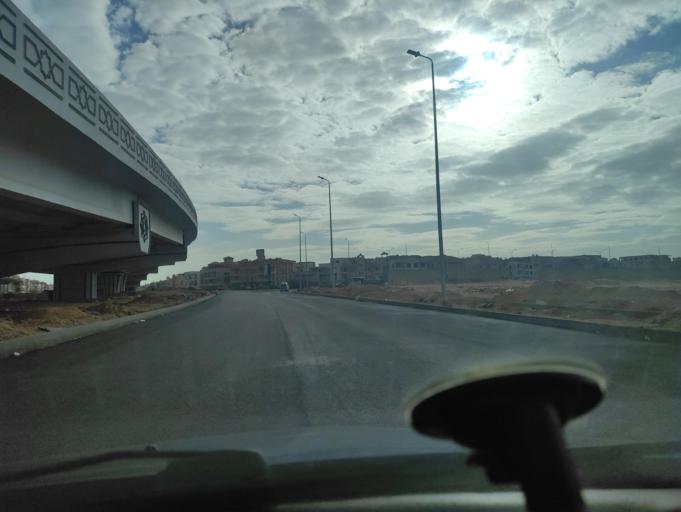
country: EG
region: Muhafazat al Qalyubiyah
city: Al Khankah
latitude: 30.0517
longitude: 31.4406
